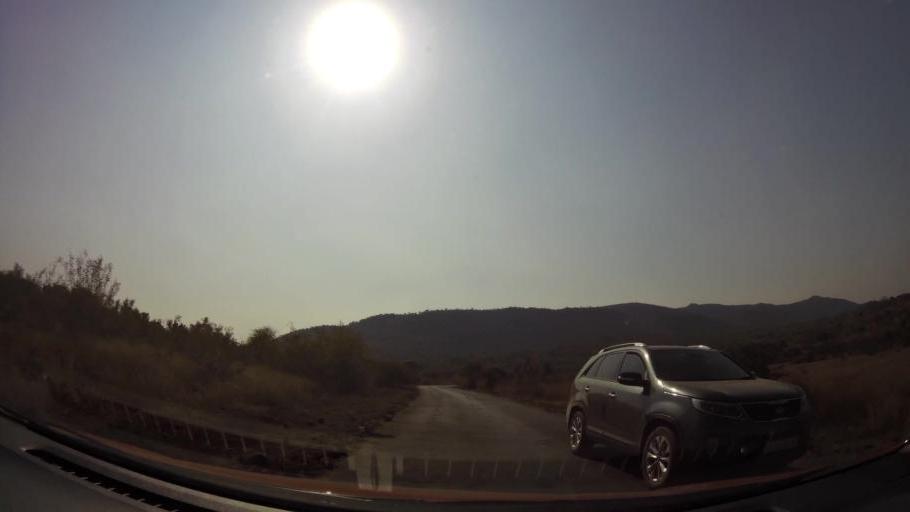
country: ZA
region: North-West
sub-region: Bojanala Platinum District Municipality
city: Mogwase
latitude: -25.3424
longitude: 27.0612
